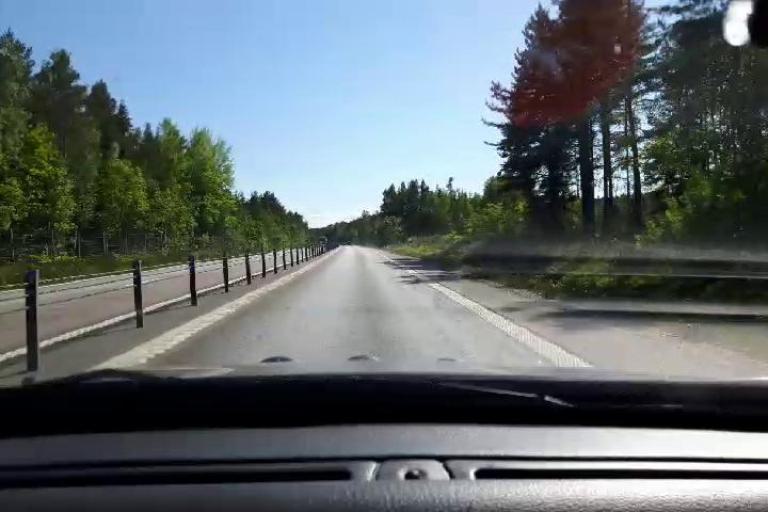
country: SE
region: Gaevleborg
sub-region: Gavle Kommun
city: Norrsundet
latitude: 60.9404
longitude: 17.0185
